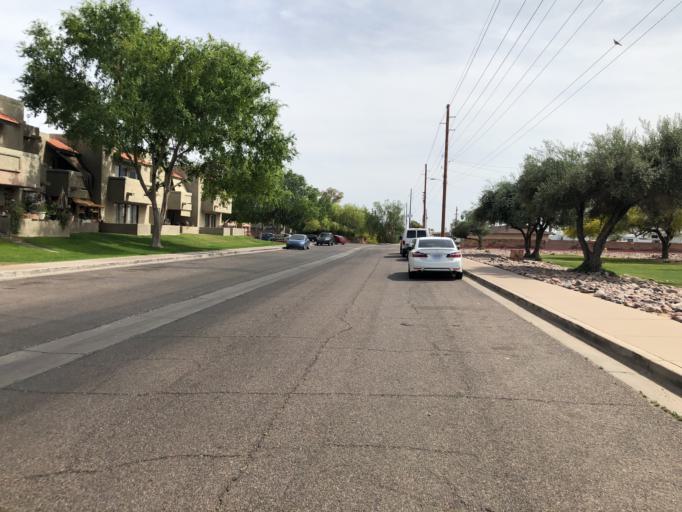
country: US
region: Arizona
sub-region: Maricopa County
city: Tempe
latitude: 33.4565
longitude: -111.9007
